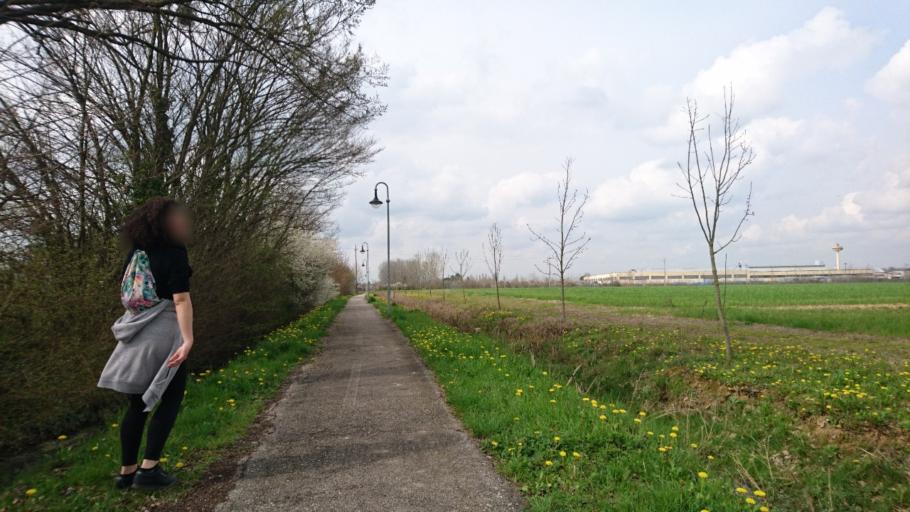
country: IT
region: Veneto
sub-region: Provincia di Padova
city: Limena
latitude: 45.4885
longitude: 11.8273
